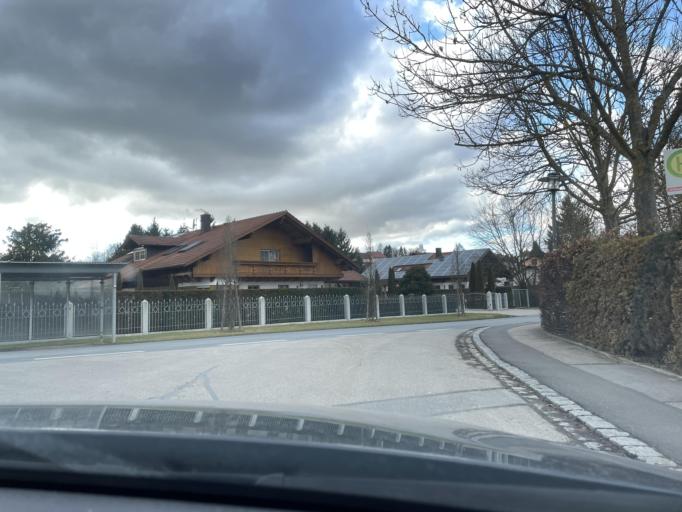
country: DE
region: Bavaria
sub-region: Upper Palatinate
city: Runding
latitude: 49.2128
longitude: 12.7684
